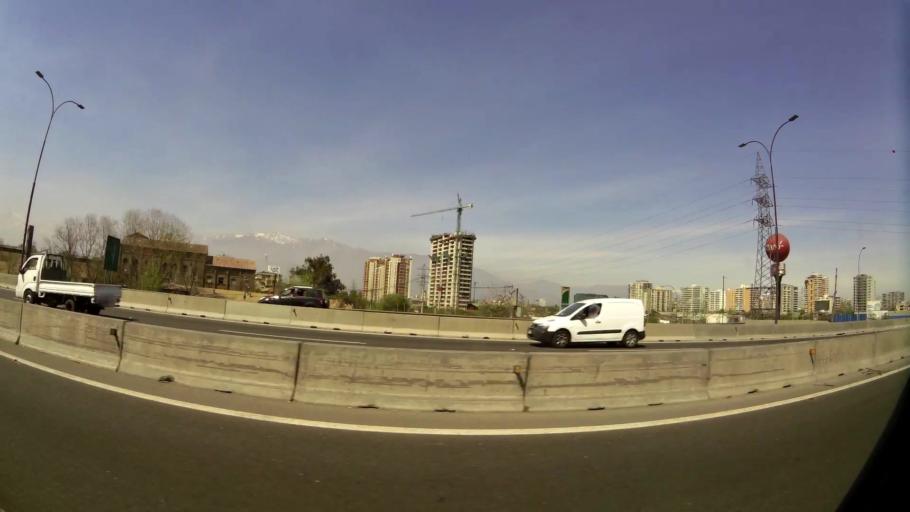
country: CL
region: Santiago Metropolitan
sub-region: Provincia de Santiago
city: Santiago
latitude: -33.4763
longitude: -70.6549
